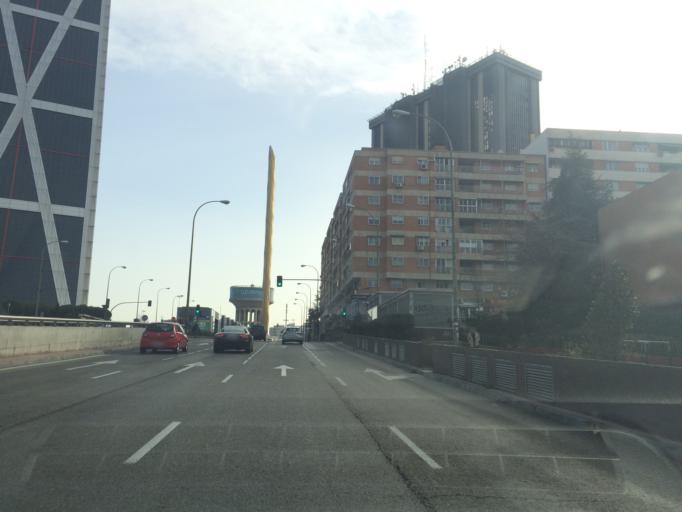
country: ES
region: Madrid
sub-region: Provincia de Madrid
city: Chamartin
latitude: 40.4673
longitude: -3.6922
